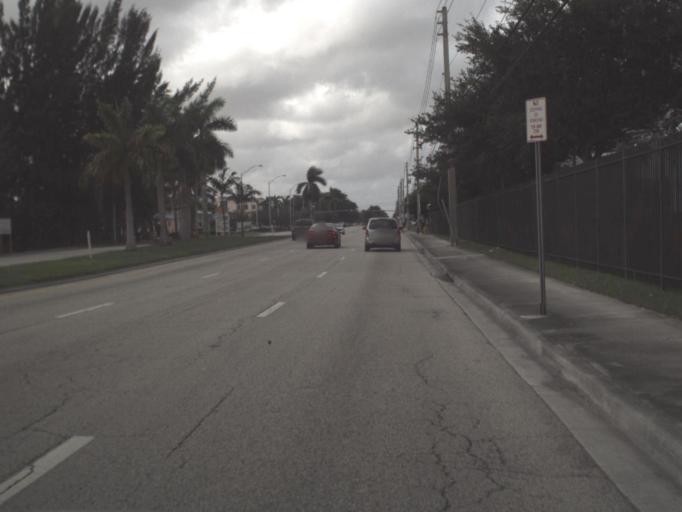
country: US
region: Florida
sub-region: Miami-Dade County
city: Doral
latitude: 25.8118
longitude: -80.3499
